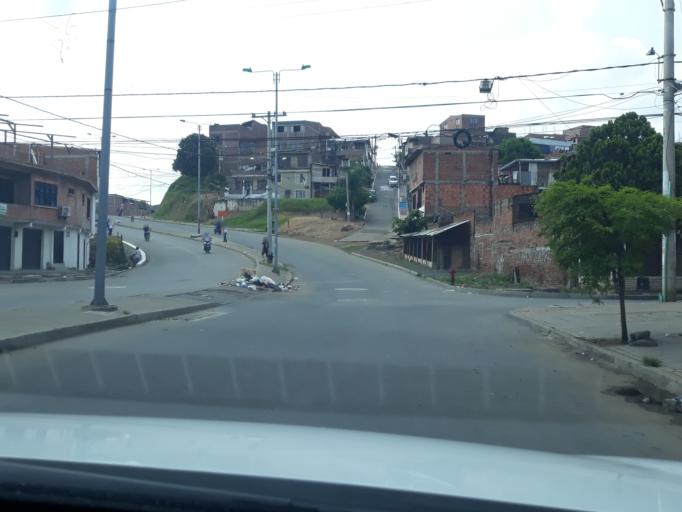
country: CO
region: Valle del Cauca
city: Cali
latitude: 3.3895
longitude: -76.5566
